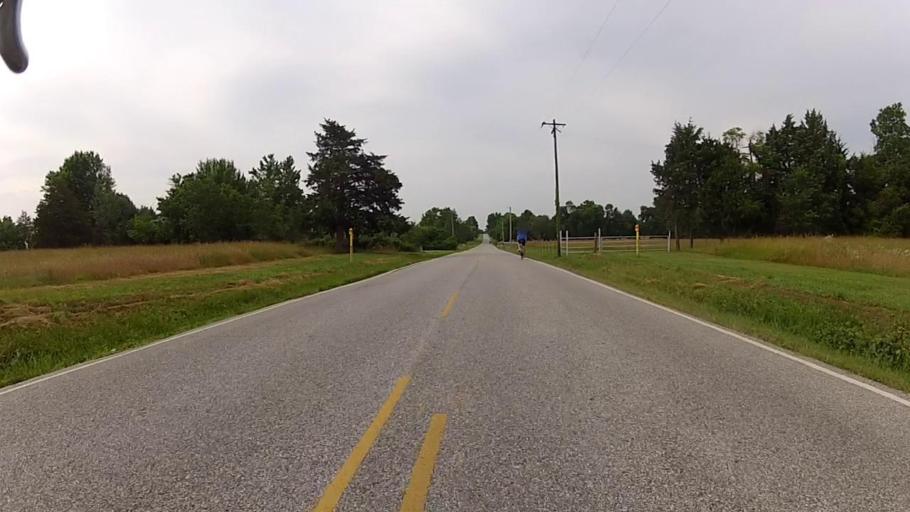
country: US
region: Kansas
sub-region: Cherokee County
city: Baxter Springs
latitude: 37.0864
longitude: -94.7224
